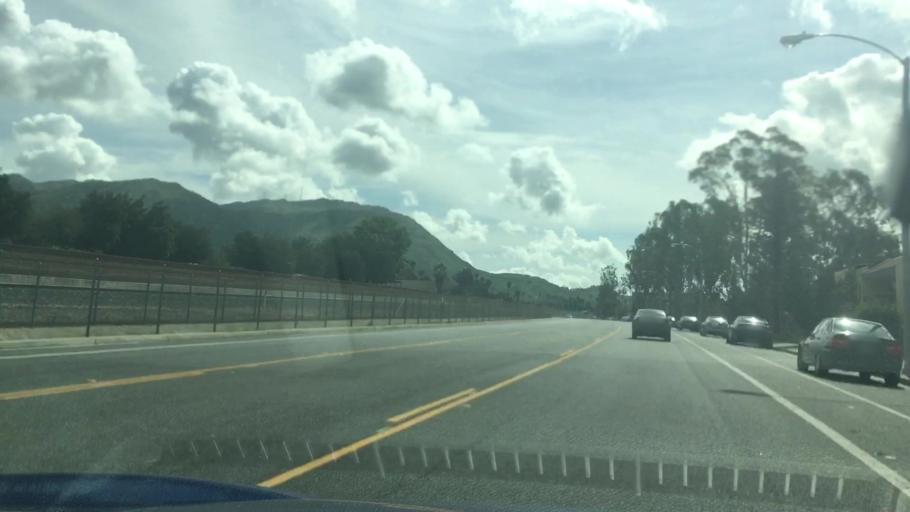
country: US
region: California
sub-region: Riverside County
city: Highgrove
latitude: 33.9867
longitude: -117.3300
